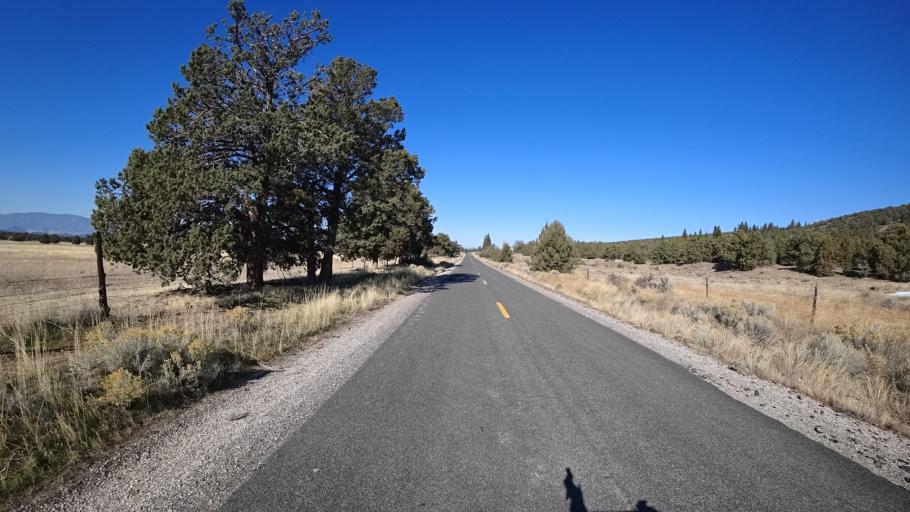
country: US
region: California
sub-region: Siskiyou County
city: Weed
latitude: 41.6187
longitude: -122.3212
